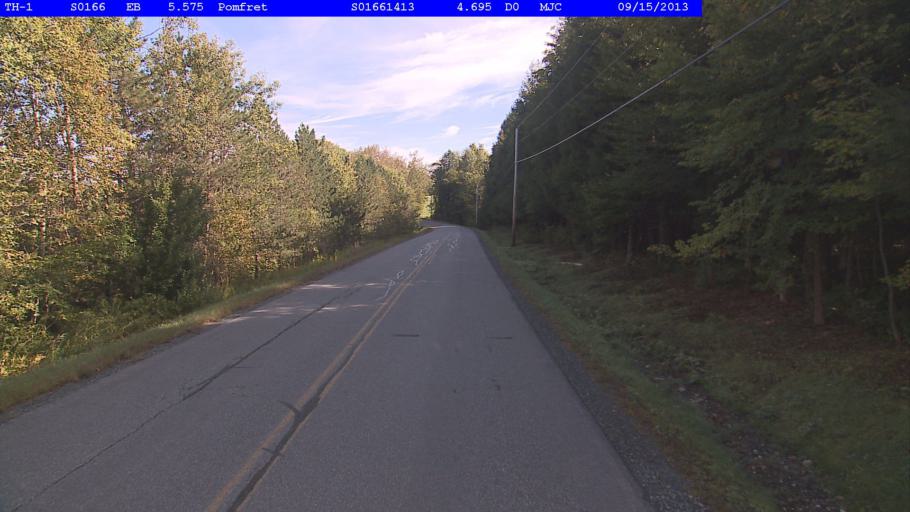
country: US
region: Vermont
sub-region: Windsor County
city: Woodstock
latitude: 43.7092
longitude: -72.5108
